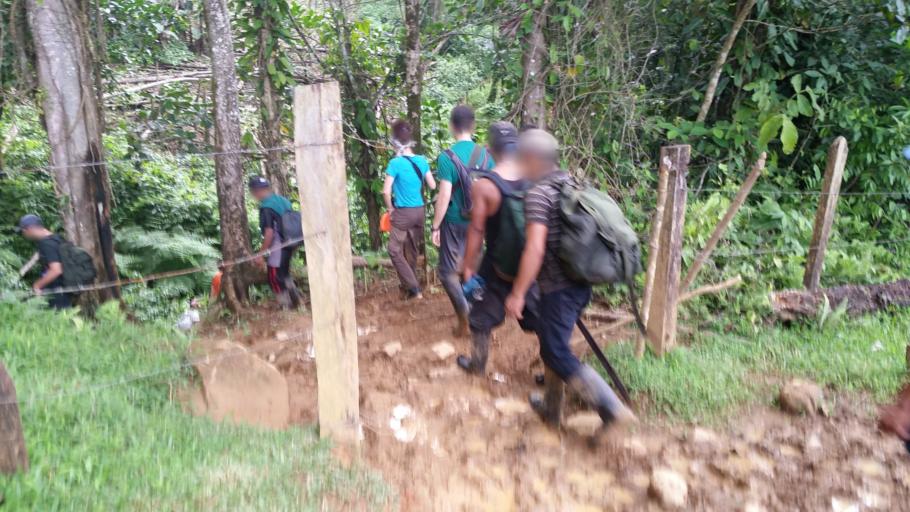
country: NI
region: Atlantico Norte (RAAN)
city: Bonanza
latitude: 13.9900
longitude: -84.7516
